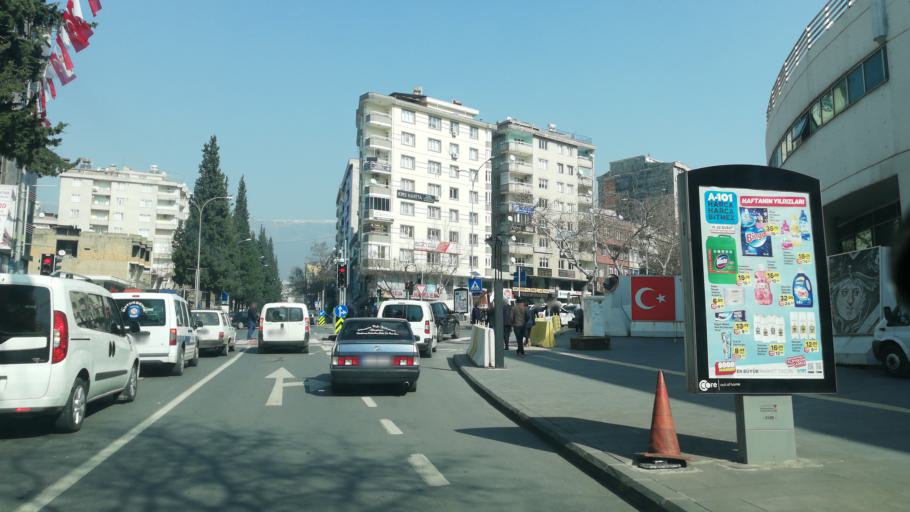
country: TR
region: Kahramanmaras
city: Kahramanmaras
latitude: 37.5770
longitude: 36.9266
